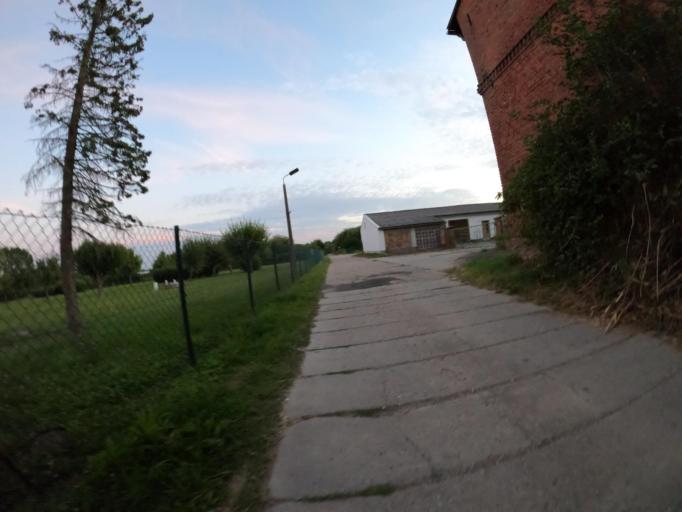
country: DE
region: Mecklenburg-Vorpommern
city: Woldegk
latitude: 53.4599
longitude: 13.5742
